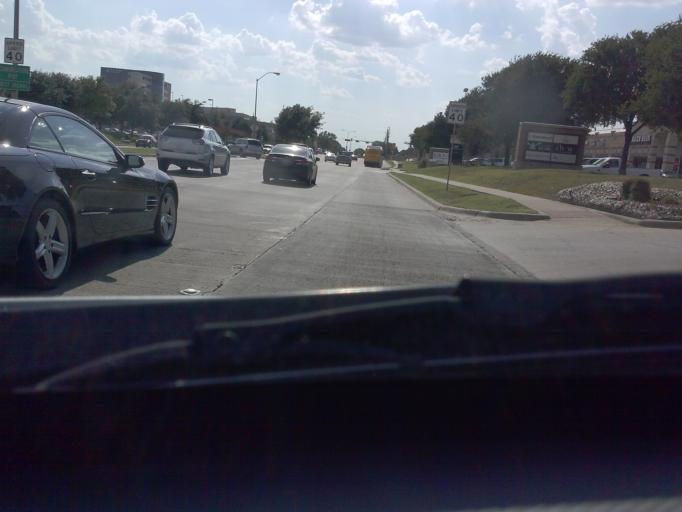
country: US
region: Texas
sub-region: Denton County
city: The Colony
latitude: 33.0453
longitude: -96.8306
